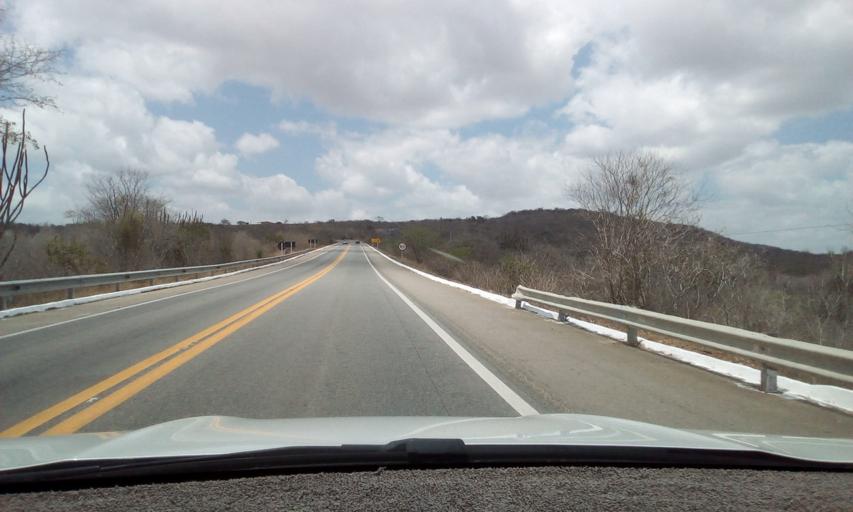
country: BR
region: Paraiba
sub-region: Boqueirao
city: Boqueirao
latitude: -7.6828
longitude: -36.0599
